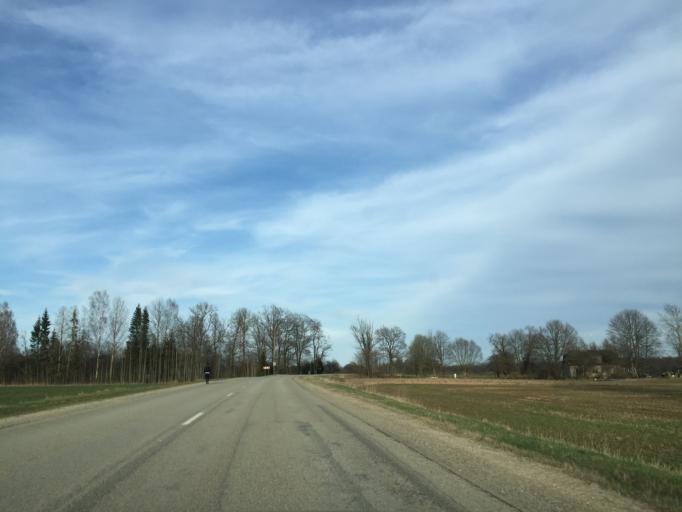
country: LV
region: Lielvarde
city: Lielvarde
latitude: 56.7980
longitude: 24.8306
